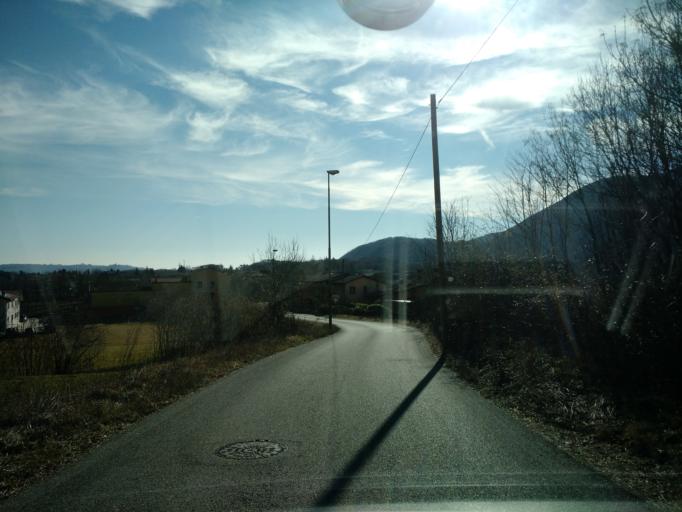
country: IT
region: Veneto
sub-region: Provincia di Vicenza
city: Cogollo del Cengio
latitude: 45.7928
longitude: 11.4040
